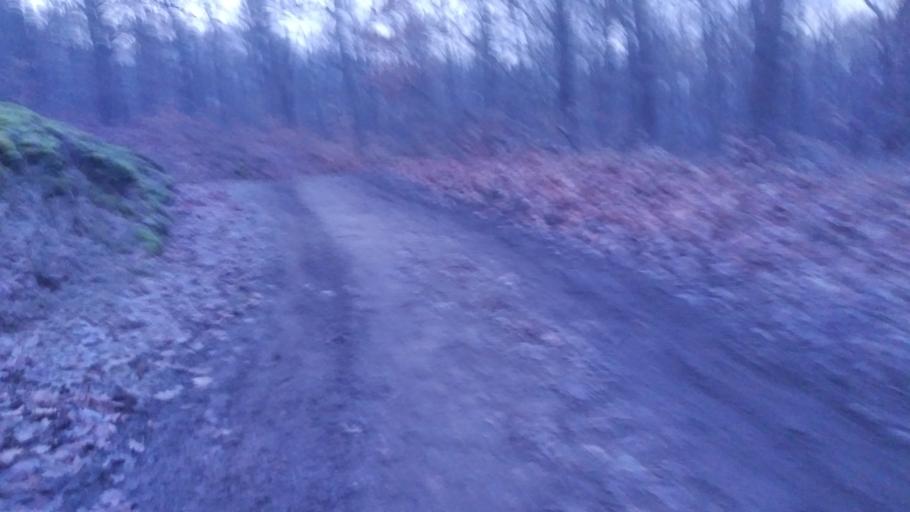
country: HU
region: Pest
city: Pilisborosjeno
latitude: 47.6132
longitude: 19.0065
